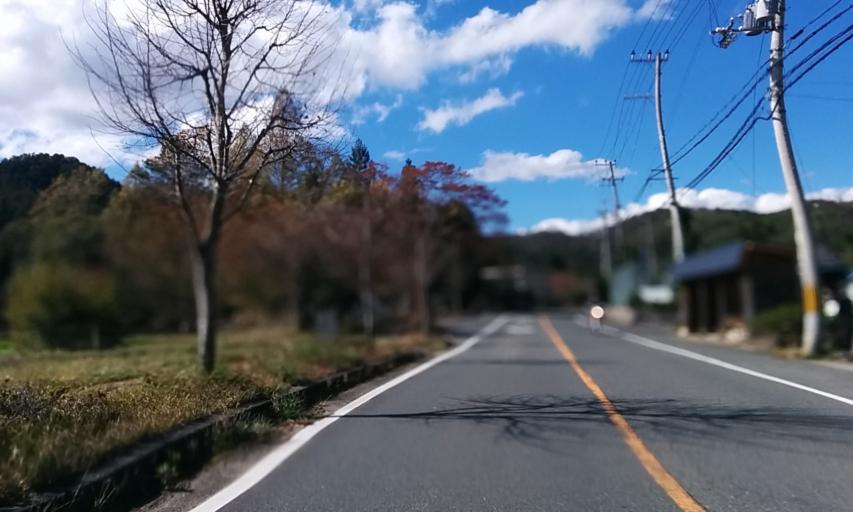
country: JP
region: Kyoto
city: Kameoka
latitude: 35.1971
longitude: 135.6347
